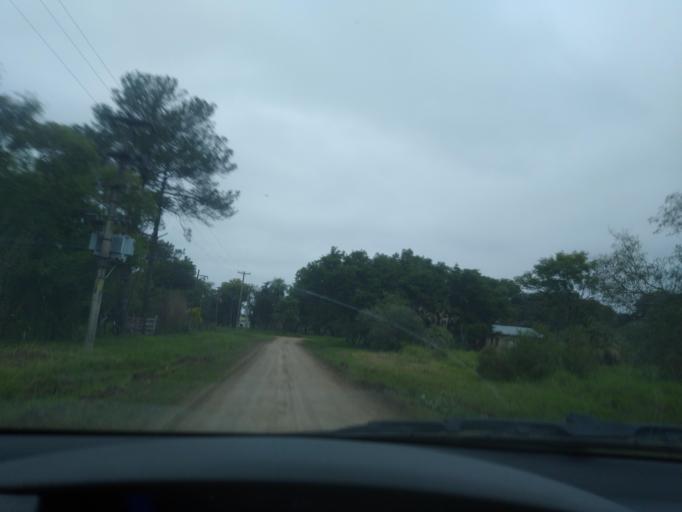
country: AR
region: Chaco
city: Colonia Benitez
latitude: -27.3328
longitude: -58.9594
